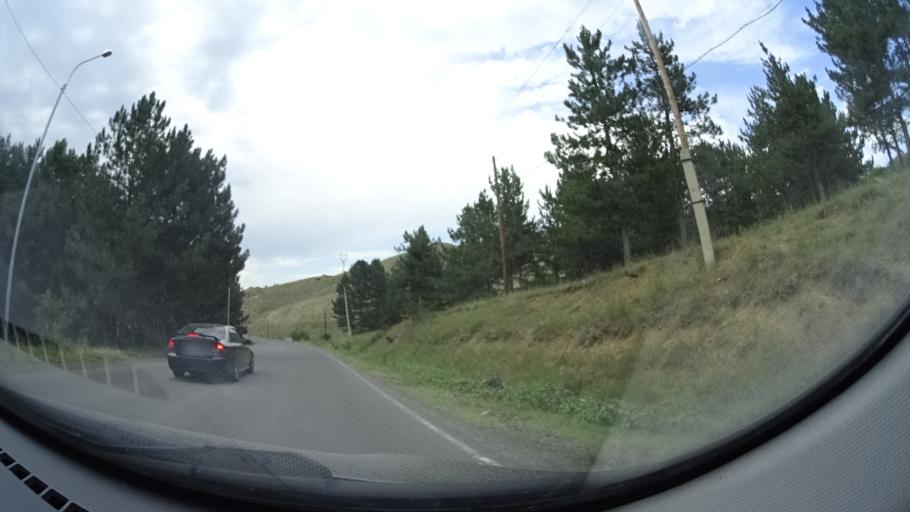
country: GE
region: Samtskhe-Javakheti
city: Aspindza
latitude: 41.5839
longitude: 43.2444
